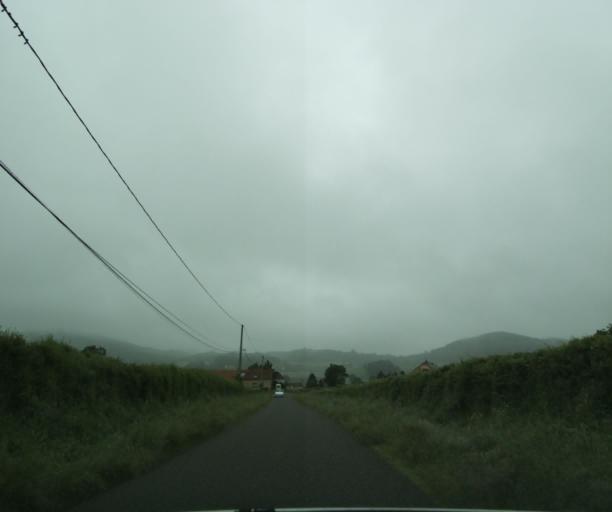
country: FR
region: Bourgogne
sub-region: Departement de Saone-et-Loire
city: Charolles
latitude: 46.4309
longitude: 4.4119
